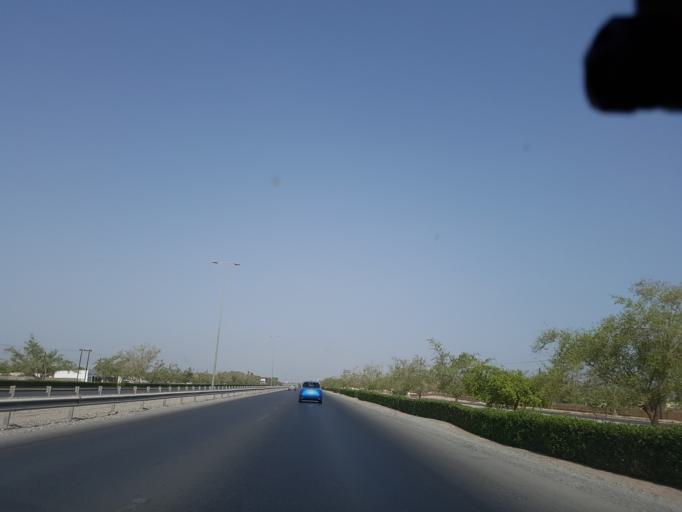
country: OM
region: Al Batinah
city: Barka'
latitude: 23.7329
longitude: 57.6912
